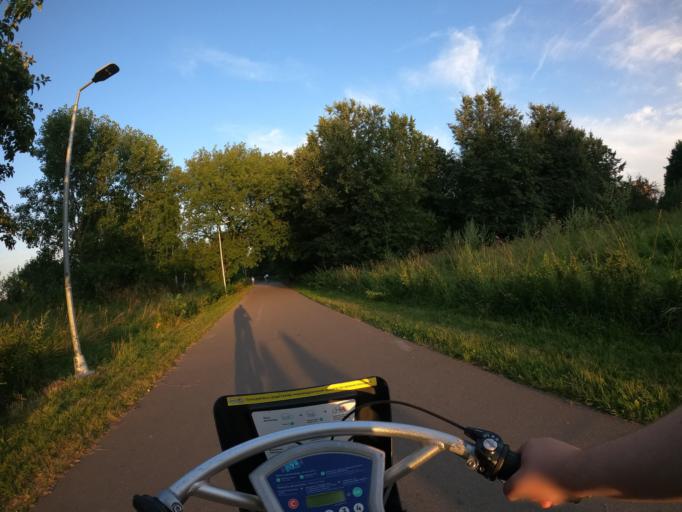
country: RU
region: Moscow
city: Strogino
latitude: 55.8101
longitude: 37.4199
